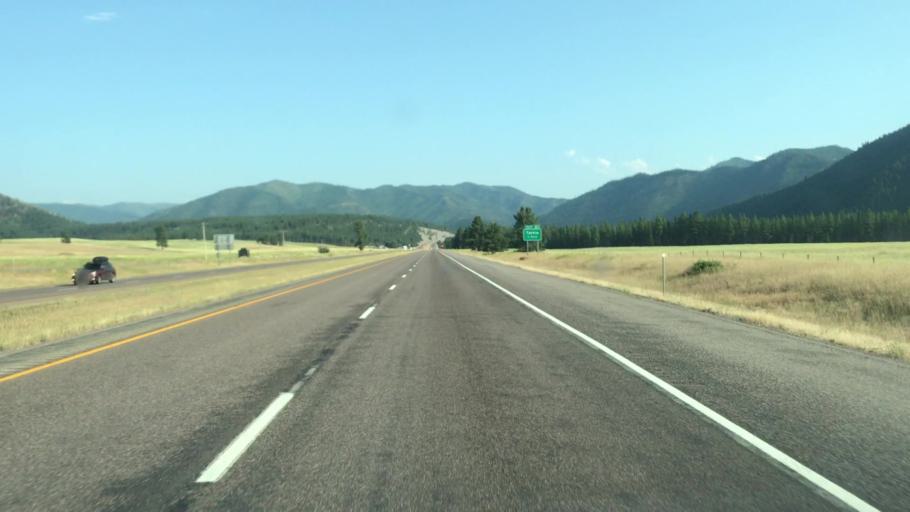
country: US
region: Montana
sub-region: Mineral County
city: Superior
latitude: 47.0430
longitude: -114.7509
